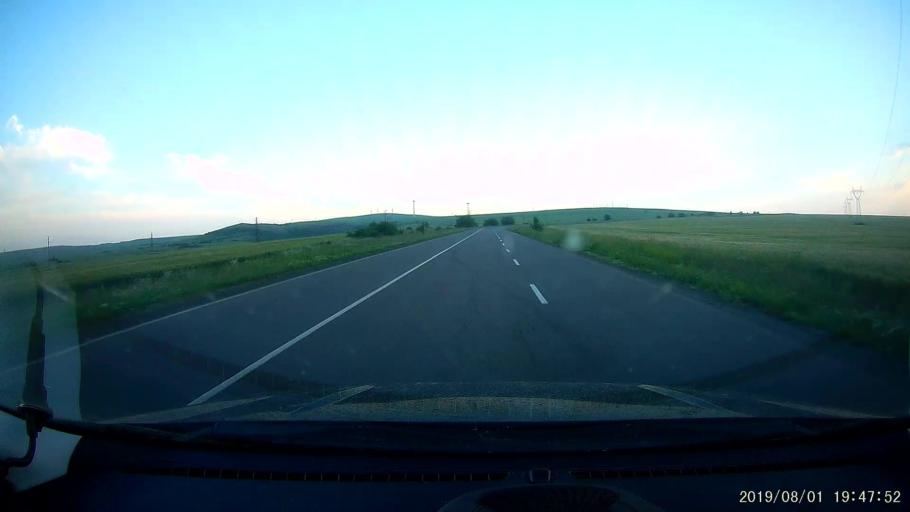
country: BG
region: Burgas
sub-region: Obshtina Karnobat
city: Karnobat
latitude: 42.6448
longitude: 26.9572
